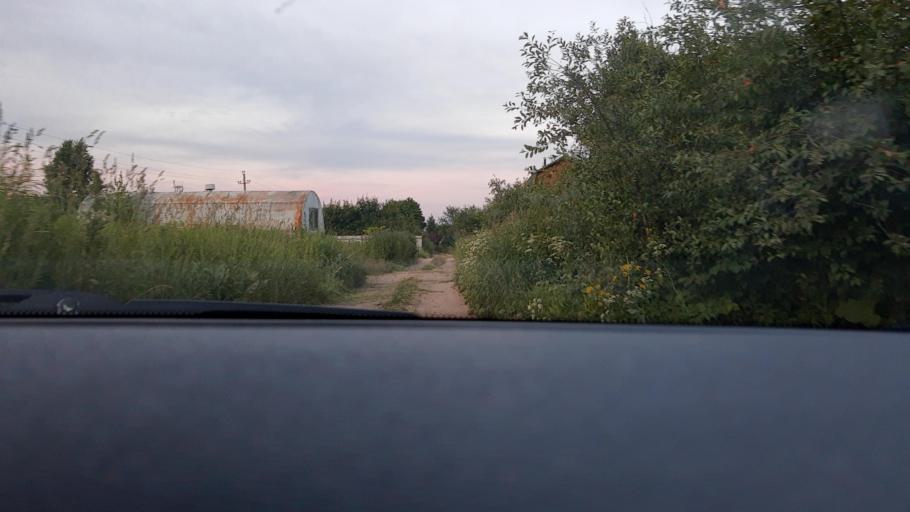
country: RU
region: Nizjnij Novgorod
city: Afonino
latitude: 56.2420
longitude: 44.0488
